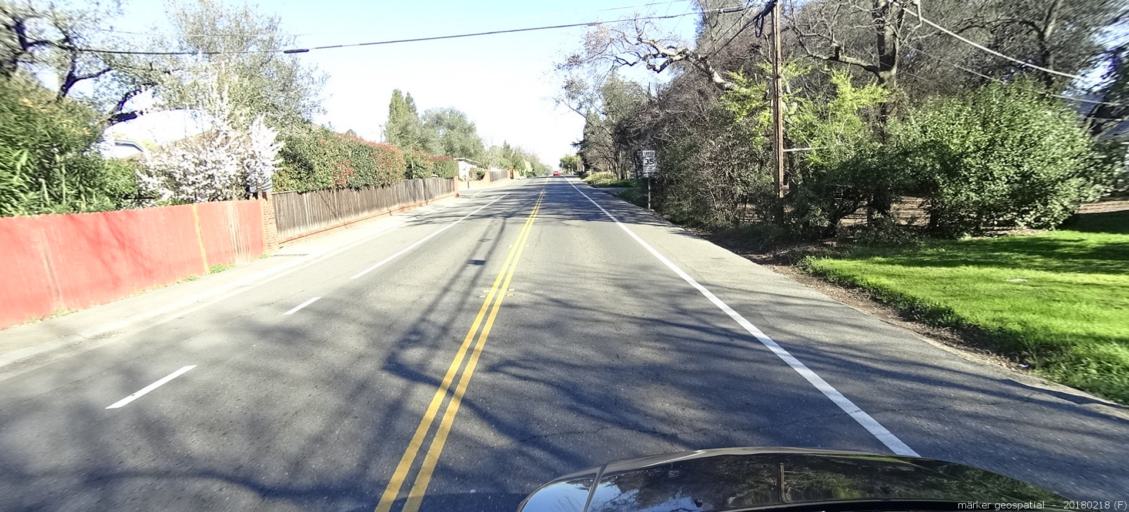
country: US
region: California
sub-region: Sacramento County
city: Orangevale
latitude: 38.6739
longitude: -121.2351
